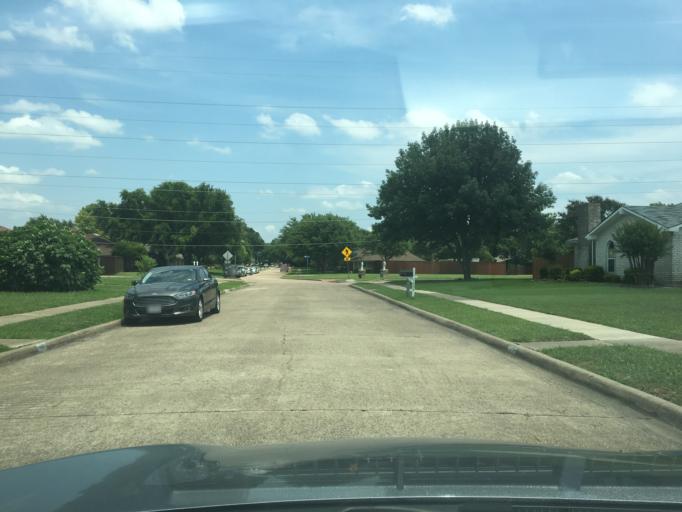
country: US
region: Texas
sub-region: Dallas County
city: Richardson
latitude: 32.9573
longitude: -96.6962
